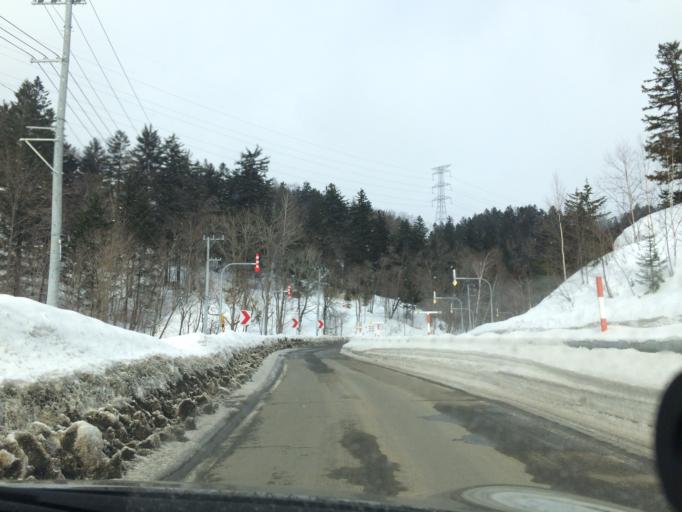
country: JP
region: Hokkaido
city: Shimo-furano
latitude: 43.0461
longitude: 142.4721
